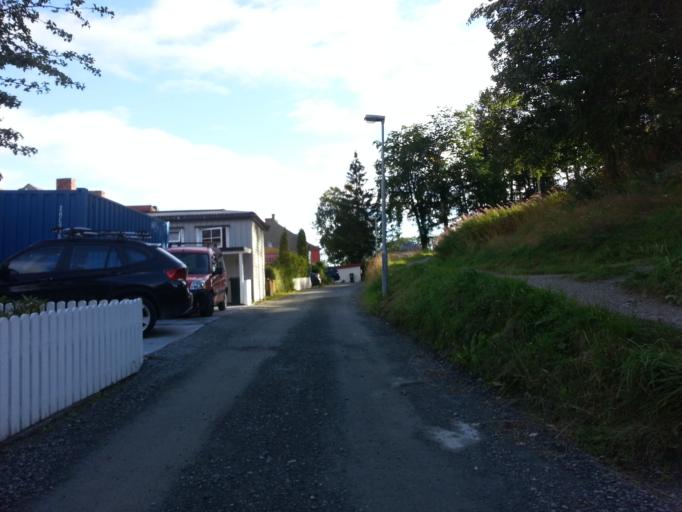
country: NO
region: Sor-Trondelag
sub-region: Trondheim
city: Trondheim
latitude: 63.4300
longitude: 10.4097
